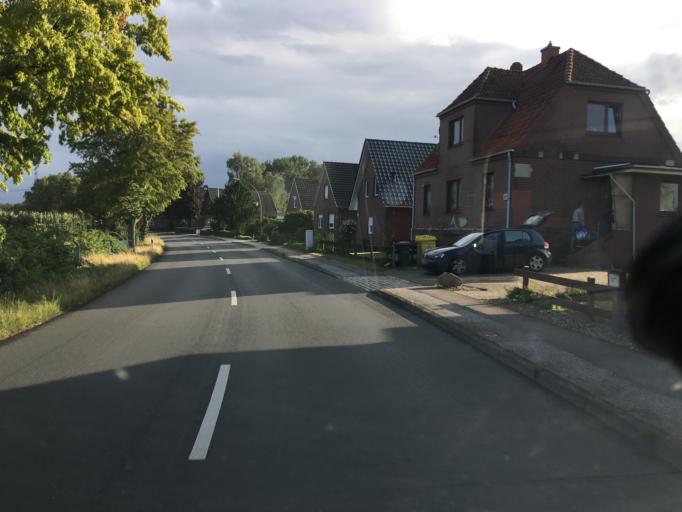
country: DE
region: Hamburg
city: Altona
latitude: 53.4982
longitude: 9.8748
